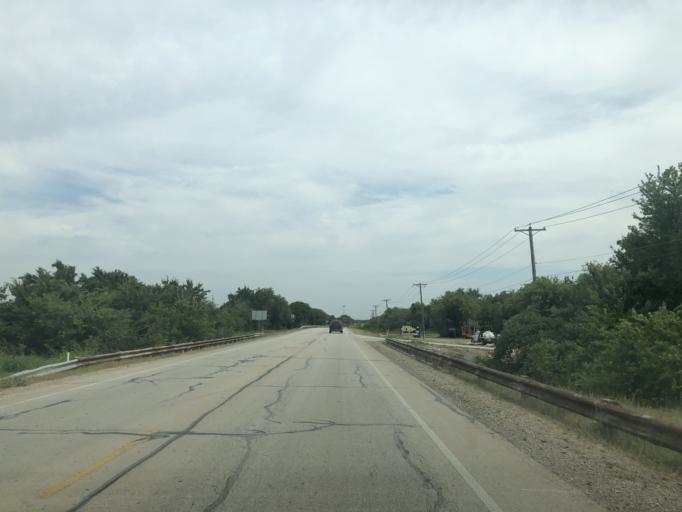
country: US
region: Texas
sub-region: Tarrant County
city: Saginaw
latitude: 32.8911
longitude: -97.3467
